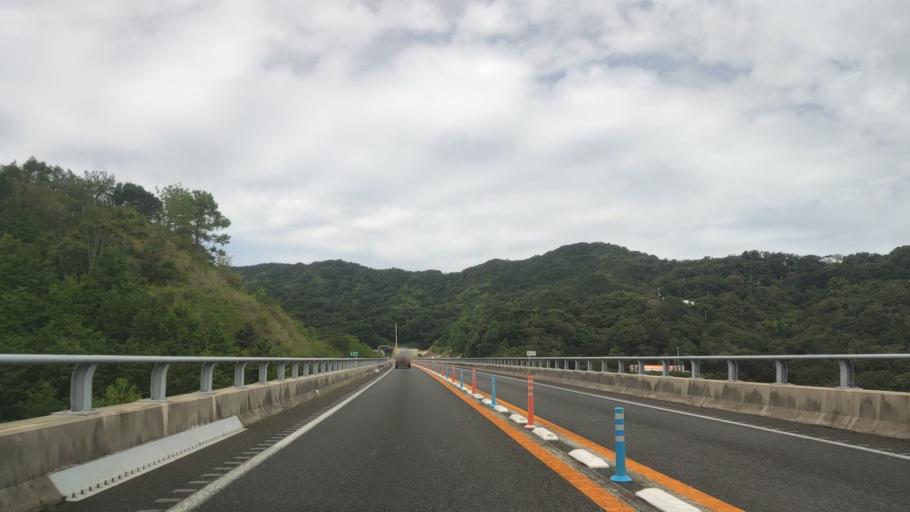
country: JP
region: Wakayama
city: Gobo
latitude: 33.8444
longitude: 135.2188
